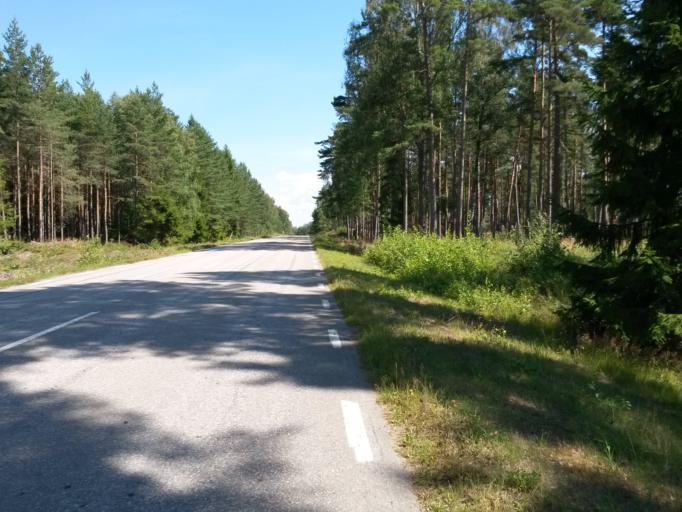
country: SE
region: Vaestra Goetaland
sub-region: Lidkopings Kommun
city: Lidkoping
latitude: 58.4476
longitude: 13.0015
